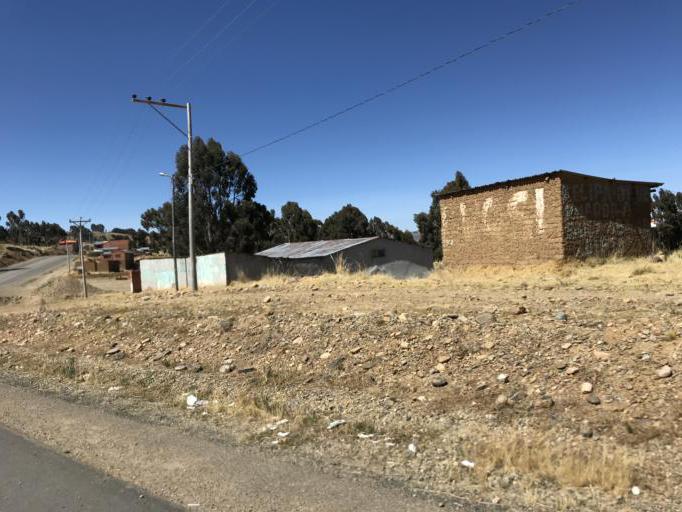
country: BO
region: La Paz
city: Huatajata
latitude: -16.2148
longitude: -68.6617
